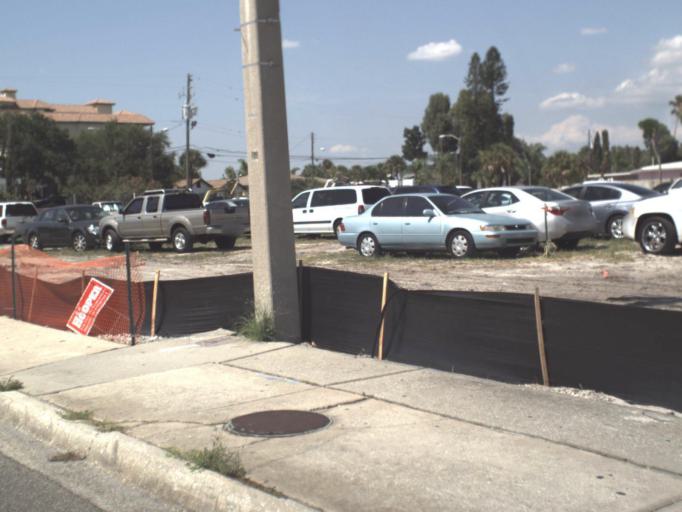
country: US
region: Florida
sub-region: Pinellas County
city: Saint Pete Beach
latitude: 27.7252
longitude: -82.7413
